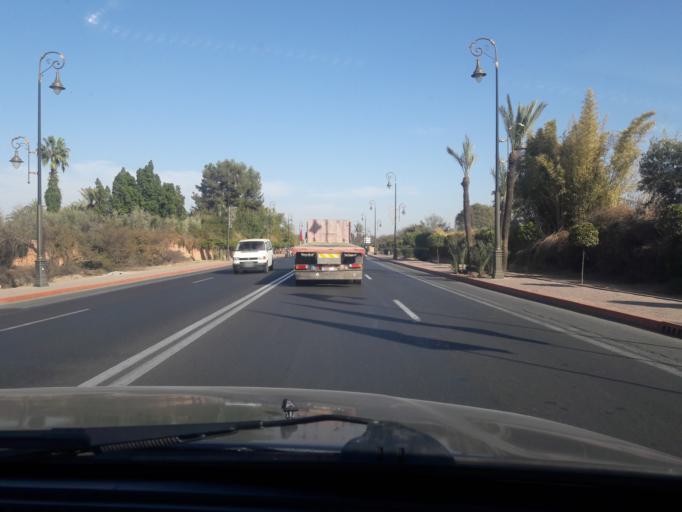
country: MA
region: Marrakech-Tensift-Al Haouz
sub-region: Marrakech
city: Marrakesh
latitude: 31.6474
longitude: -7.9688
